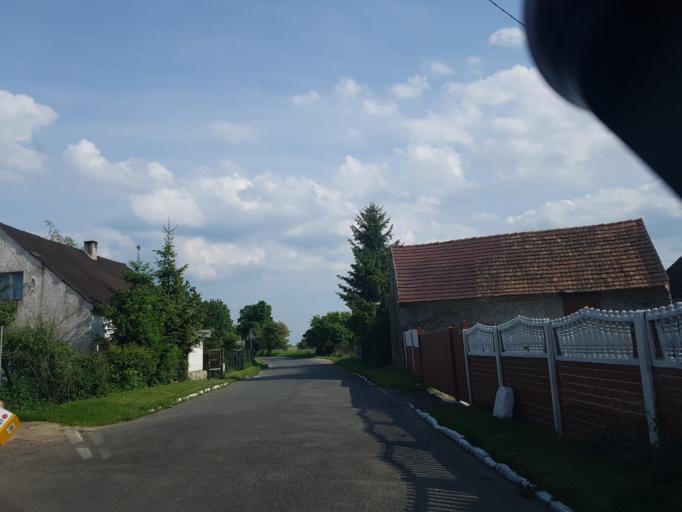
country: PL
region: Lower Silesian Voivodeship
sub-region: Powiat olawski
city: Wierzbno
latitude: 50.8919
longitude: 17.1312
